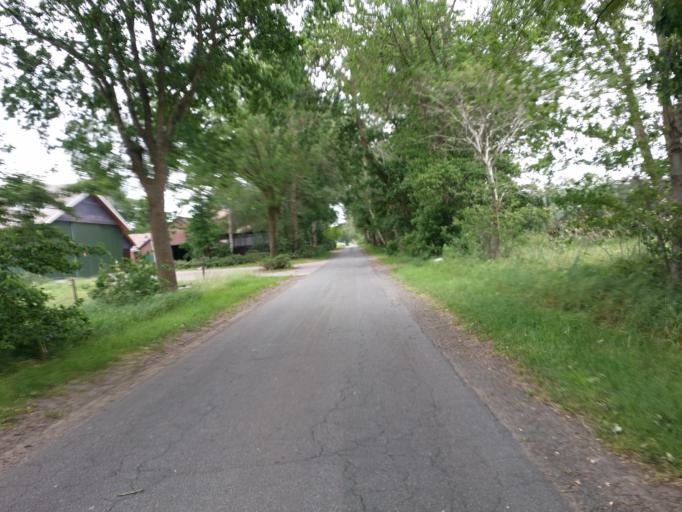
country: DE
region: Lower Saxony
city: Bockhorn
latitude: 53.3220
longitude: 8.0380
